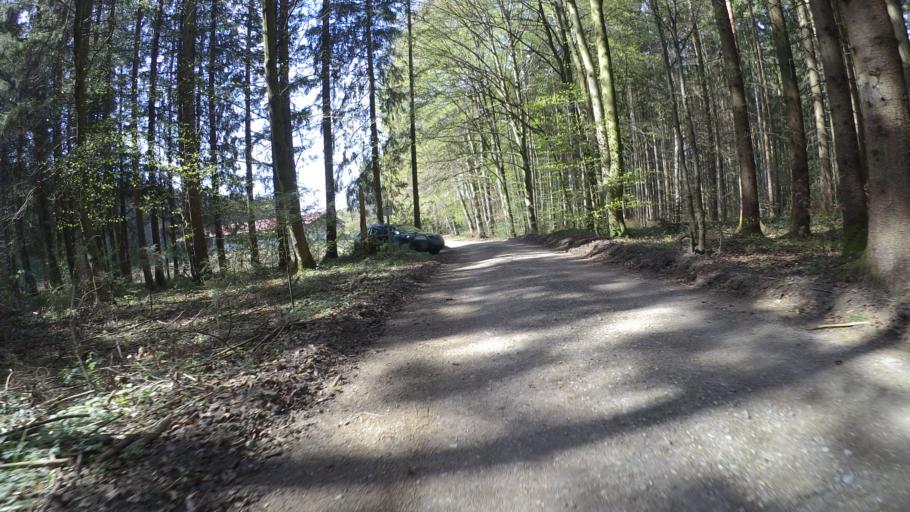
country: DE
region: Bavaria
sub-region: Upper Bavaria
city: Nussdorf
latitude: 47.9171
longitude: 12.5789
